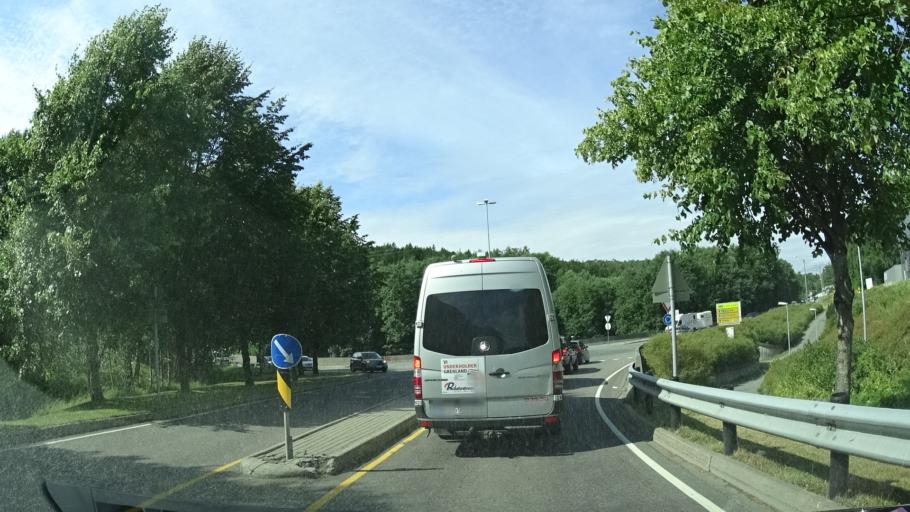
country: NO
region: Telemark
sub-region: Porsgrunn
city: Porsgrunn
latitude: 59.0751
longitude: 9.6833
